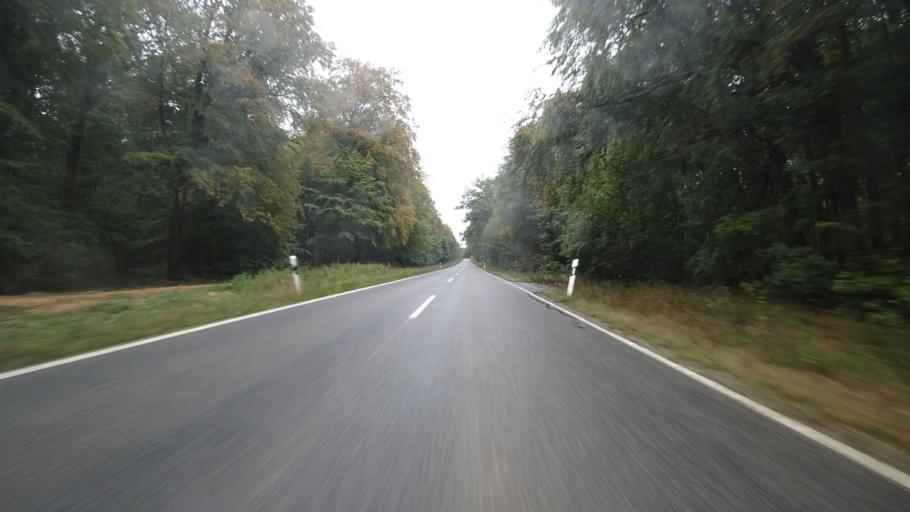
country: DE
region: Rheinland-Pfalz
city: Rheinbollen
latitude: 50.0076
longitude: 7.6466
